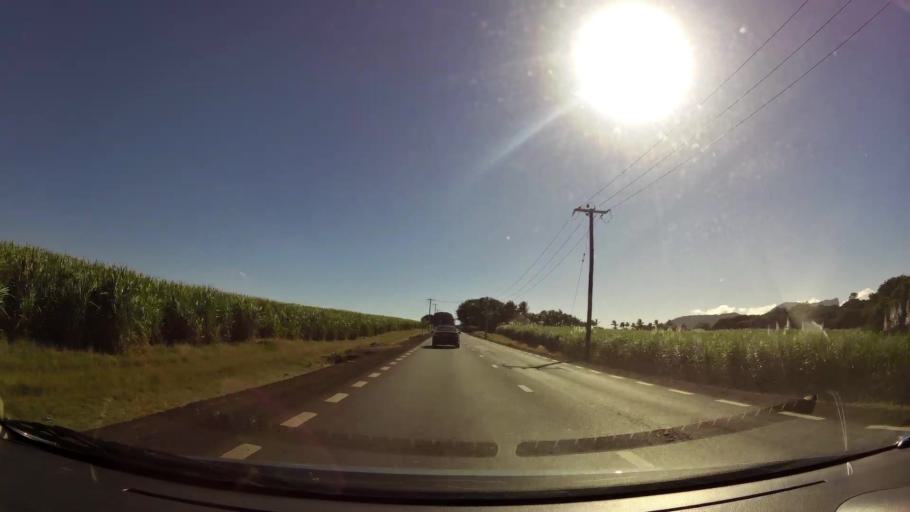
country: MU
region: Black River
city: Cascavelle
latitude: -20.2934
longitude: 57.4018
